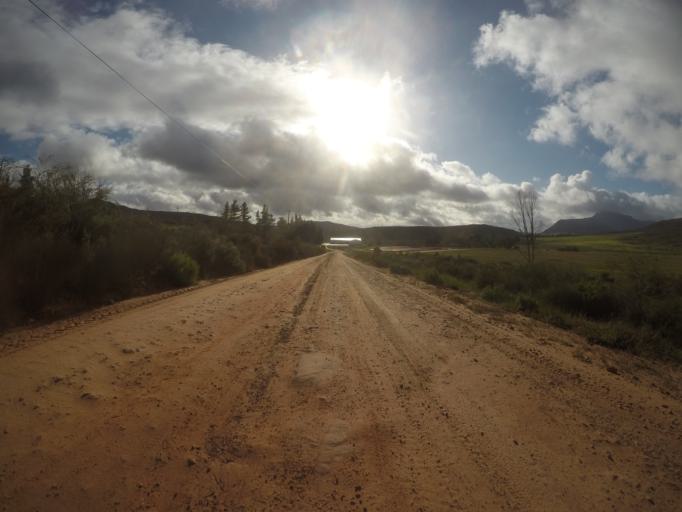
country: ZA
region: Western Cape
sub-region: West Coast District Municipality
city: Clanwilliam
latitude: -32.3425
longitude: 18.8301
